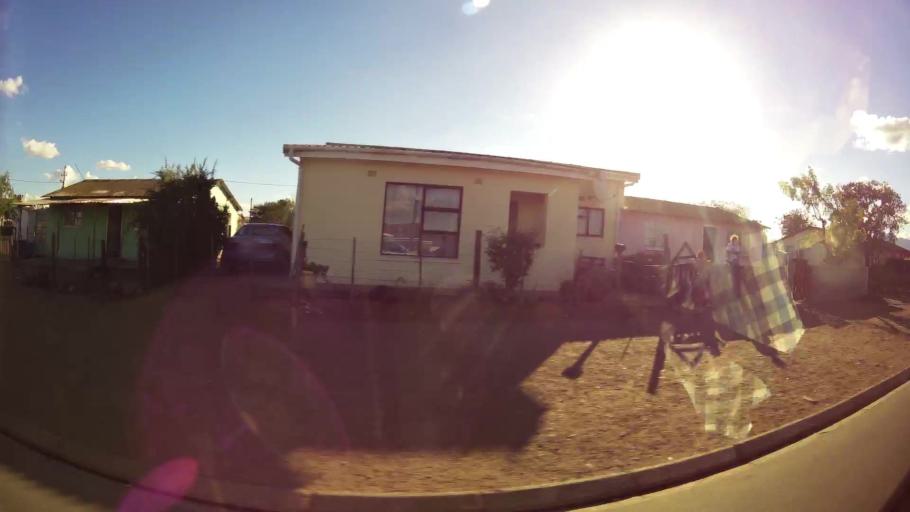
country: ZA
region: Western Cape
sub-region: Eden District Municipality
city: Riversdale
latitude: -34.1054
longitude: 20.9665
